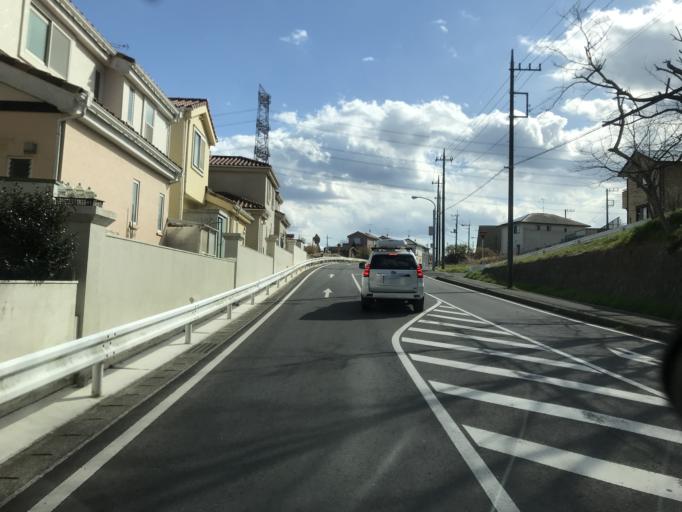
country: JP
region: Chiba
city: Katori-shi
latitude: 35.8892
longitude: 140.4122
